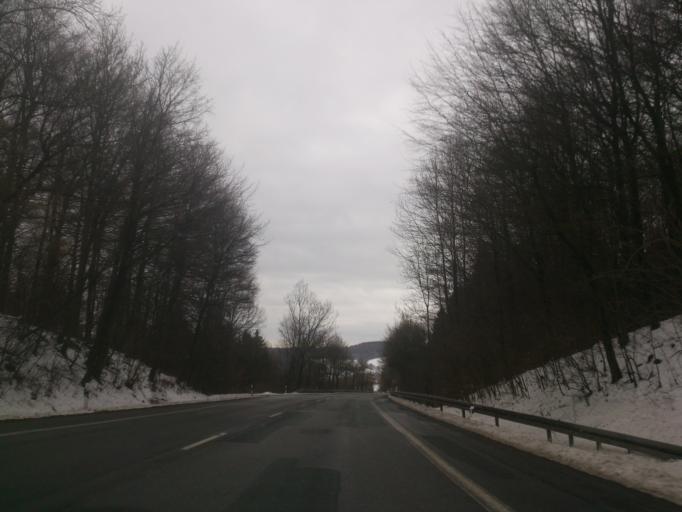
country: DE
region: North Rhine-Westphalia
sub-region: Regierungsbezirk Detmold
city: Bad Driburg
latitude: 51.6847
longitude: 8.9821
